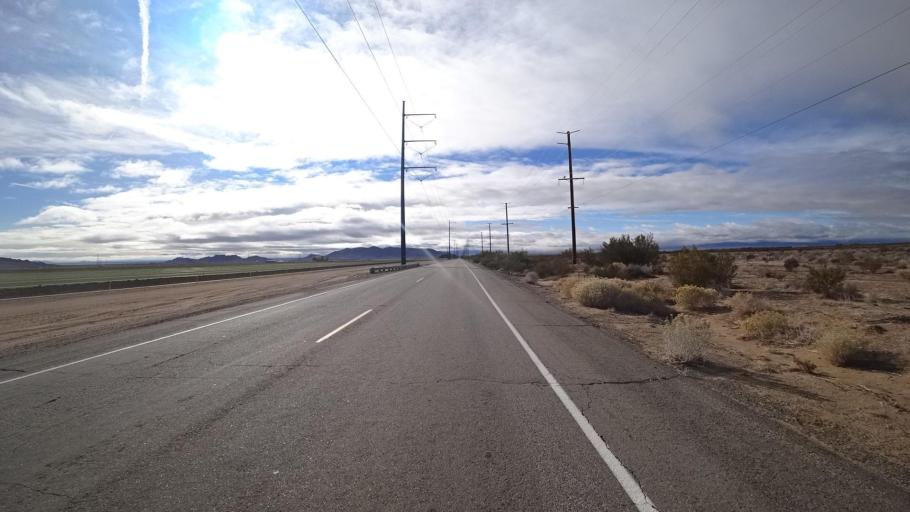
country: US
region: California
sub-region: Kern County
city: Rosamond
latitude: 34.9351
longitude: -118.2916
